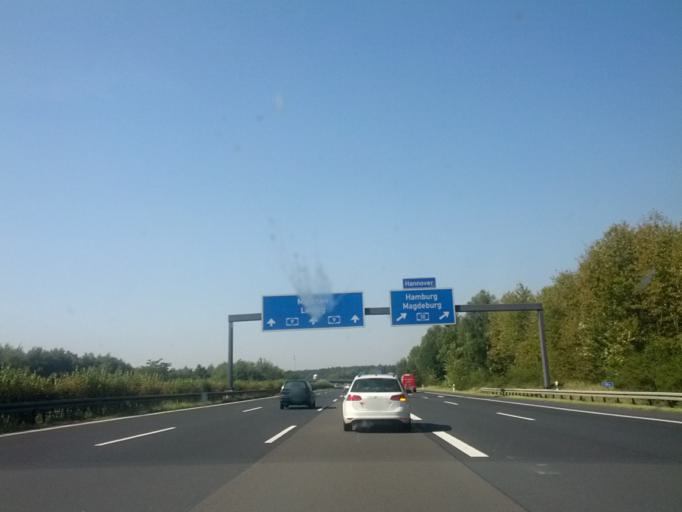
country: DE
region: Brandenburg
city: Fichtenwalde
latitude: 52.2924
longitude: 12.9261
